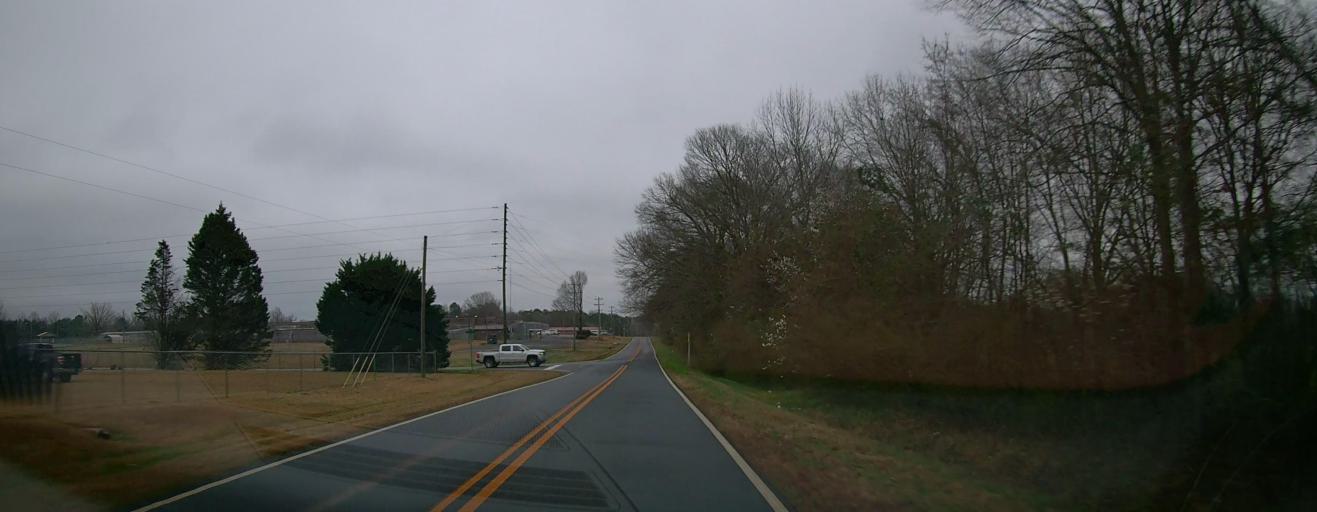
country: US
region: Georgia
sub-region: Pike County
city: Zebulon
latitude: 33.1153
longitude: -84.3631
